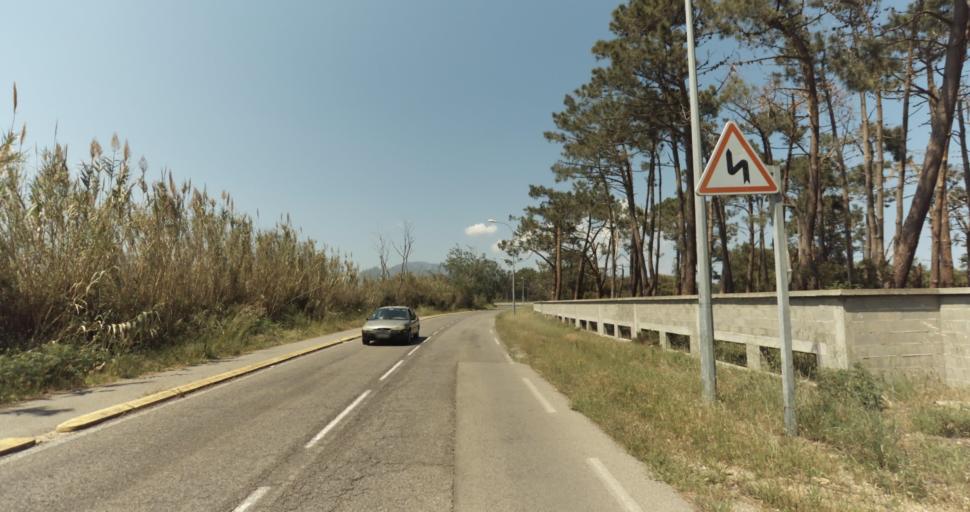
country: FR
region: Corsica
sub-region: Departement de la Haute-Corse
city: Biguglia
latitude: 42.6204
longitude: 9.4746
